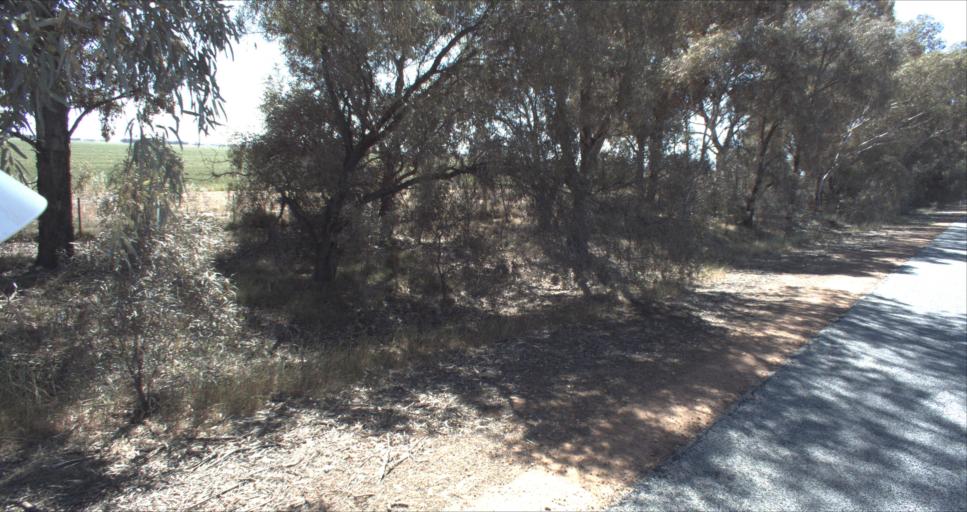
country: AU
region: New South Wales
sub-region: Leeton
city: Leeton
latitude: -34.5785
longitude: 146.2691
